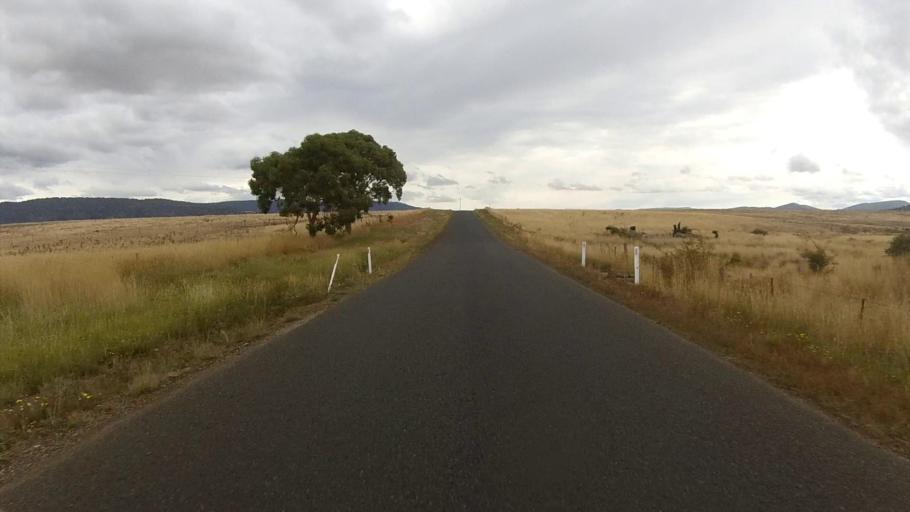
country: AU
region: Tasmania
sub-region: Northern Midlands
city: Evandale
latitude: -41.8276
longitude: 147.7881
